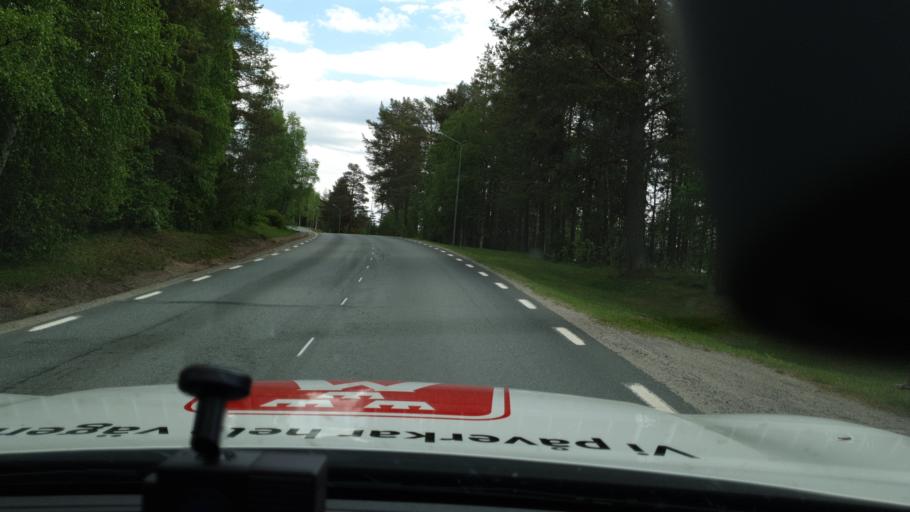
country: SE
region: Vaesterbotten
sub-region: Sorsele Kommun
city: Sorsele
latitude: 65.3364
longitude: 17.5912
